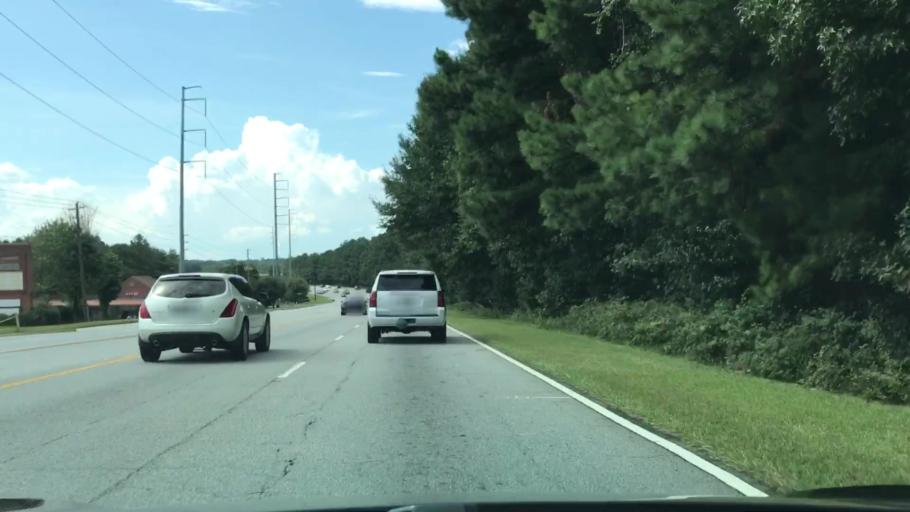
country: US
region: Georgia
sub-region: Gwinnett County
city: Duluth
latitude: 34.0029
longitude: -84.1644
